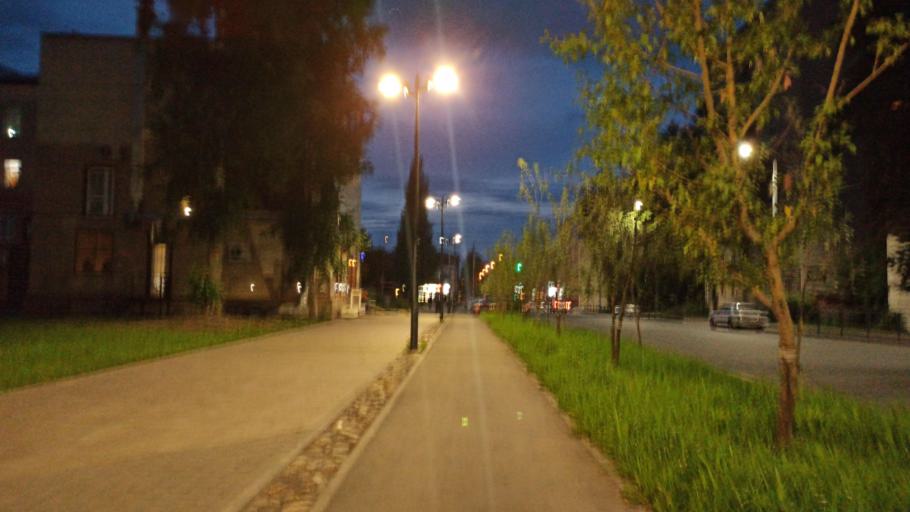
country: RU
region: Tomsk
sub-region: Tomskiy Rayon
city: Tomsk
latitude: 56.4639
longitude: 84.9595
